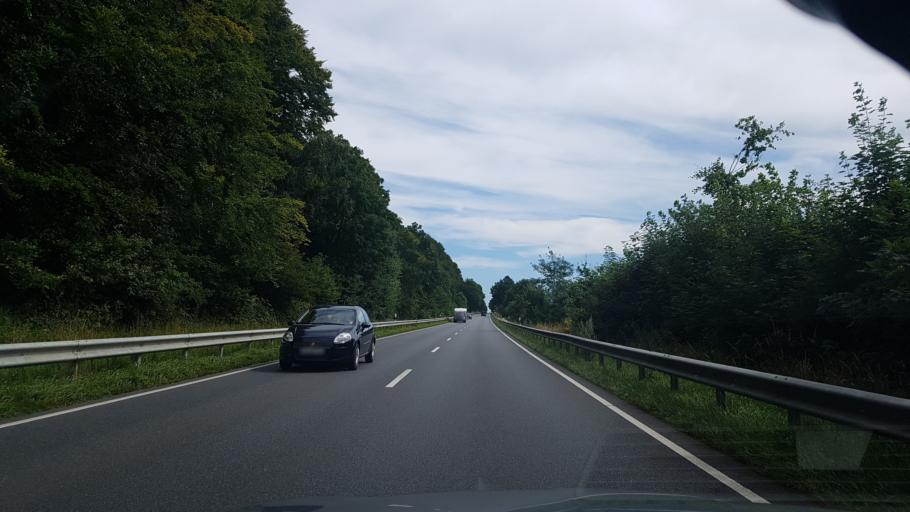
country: DE
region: Schleswig-Holstein
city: Schonbek
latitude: 54.1831
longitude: 9.9661
